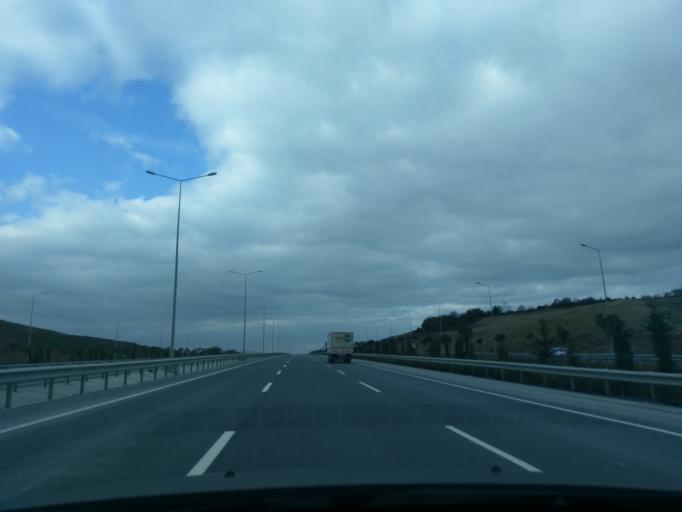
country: TR
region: Istanbul
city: Durusu
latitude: 41.2425
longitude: 28.7876
